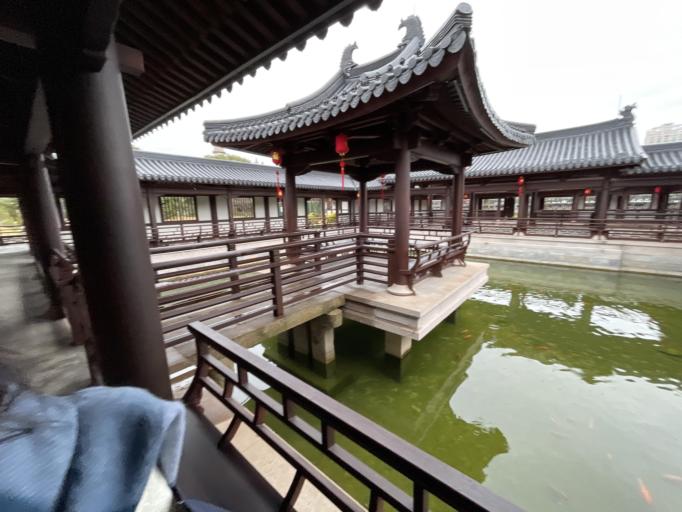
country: CN
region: Zhejiang Sheng
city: Louqiao
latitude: 28.0305
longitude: 120.6395
